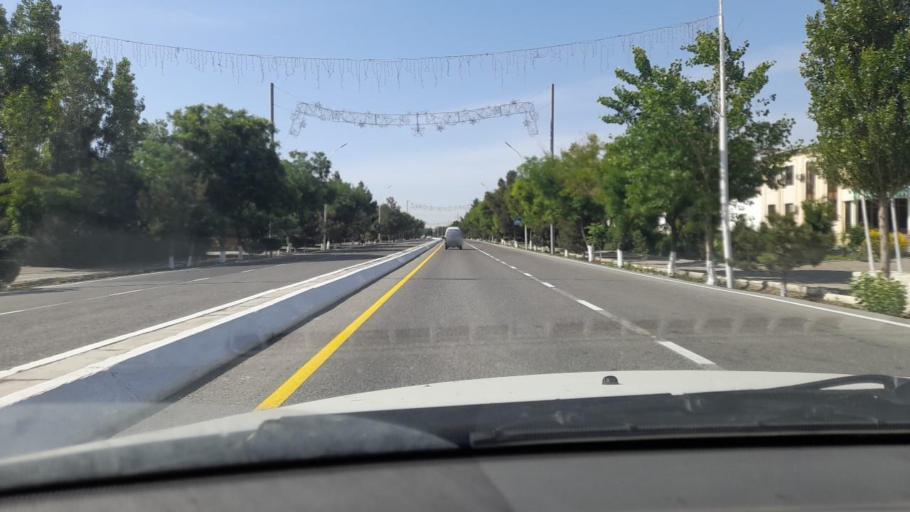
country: UZ
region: Bukhara
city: Bukhara
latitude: 39.7937
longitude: 64.4340
